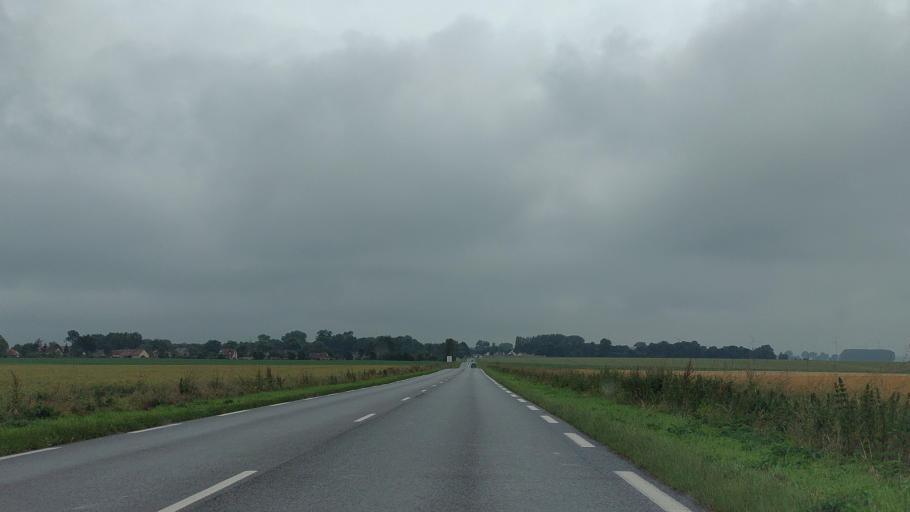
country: FR
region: Picardie
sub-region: Departement de la Somme
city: Chepy
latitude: 50.0831
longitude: 1.6452
